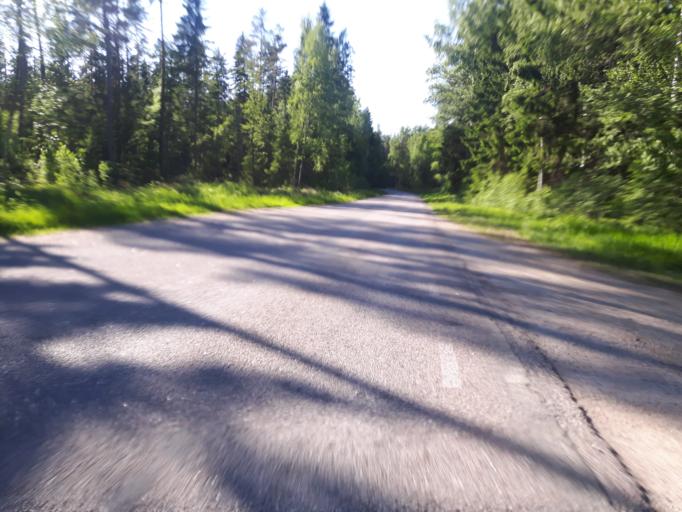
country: EE
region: Harju
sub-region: Loksa linn
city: Loksa
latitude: 59.5657
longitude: 25.9748
